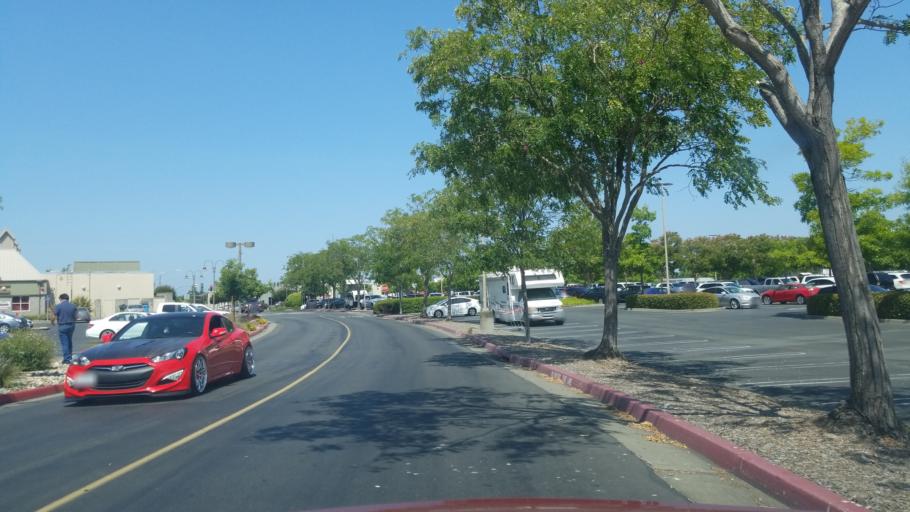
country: US
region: California
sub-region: Sonoma County
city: Roseland
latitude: 38.4185
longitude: -122.7113
